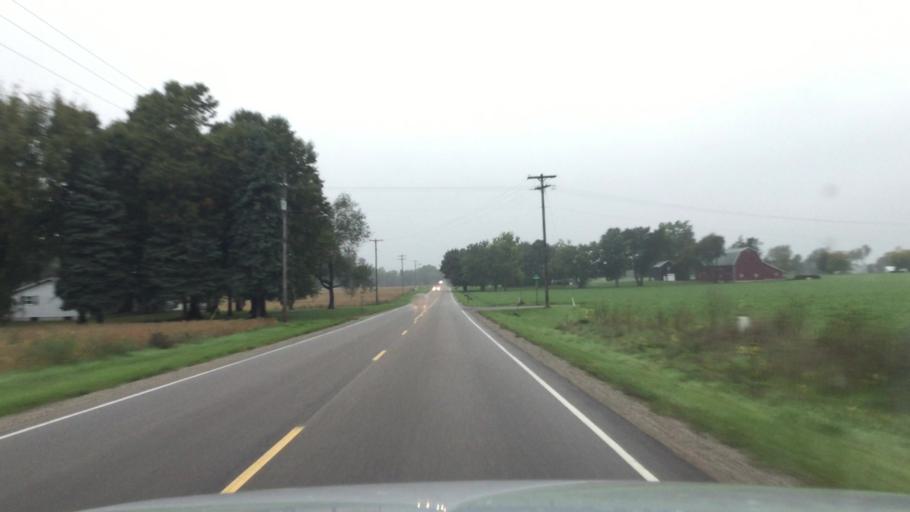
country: US
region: Michigan
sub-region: Shiawassee County
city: Corunna
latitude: 42.8968
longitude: -84.1028
